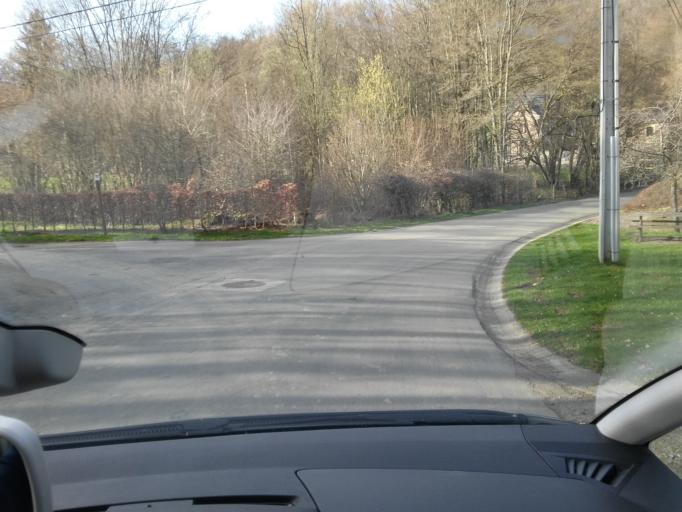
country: BE
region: Wallonia
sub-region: Province du Luxembourg
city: Daverdisse
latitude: 49.9907
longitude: 5.1579
